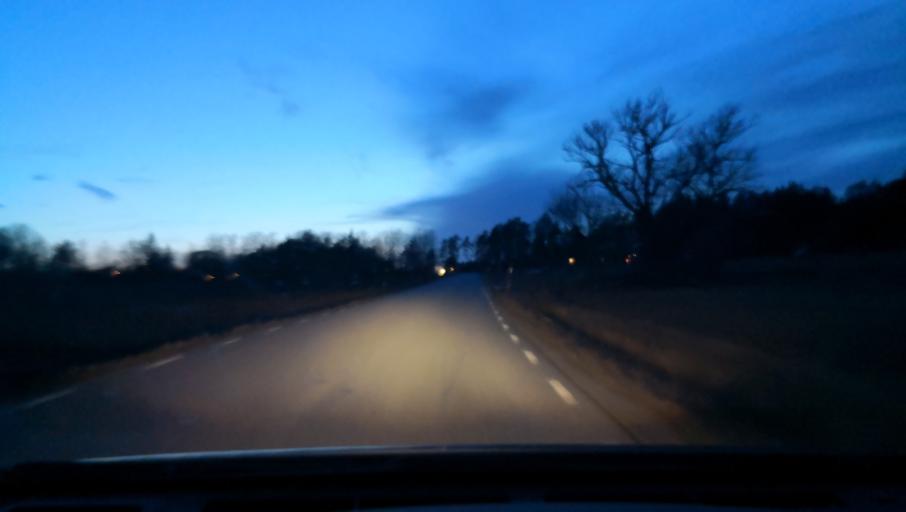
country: SE
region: Uppsala
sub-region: Enkopings Kommun
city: Grillby
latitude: 59.6065
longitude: 17.2873
